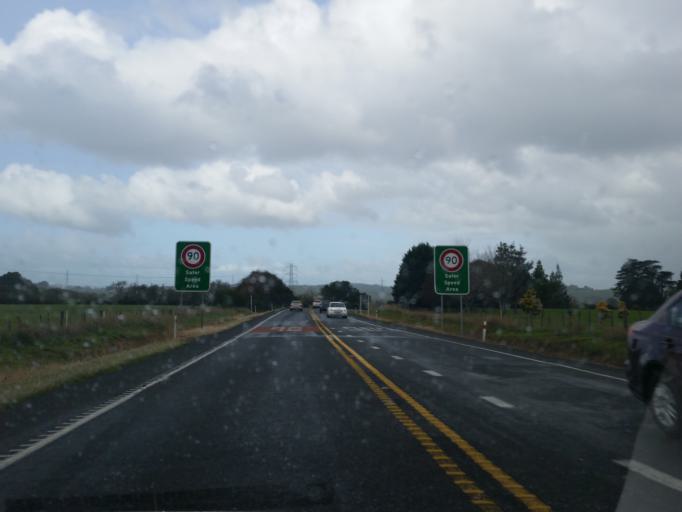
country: NZ
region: Waikato
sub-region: Waikato District
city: Te Kauwhata
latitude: -37.2352
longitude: 175.1684
